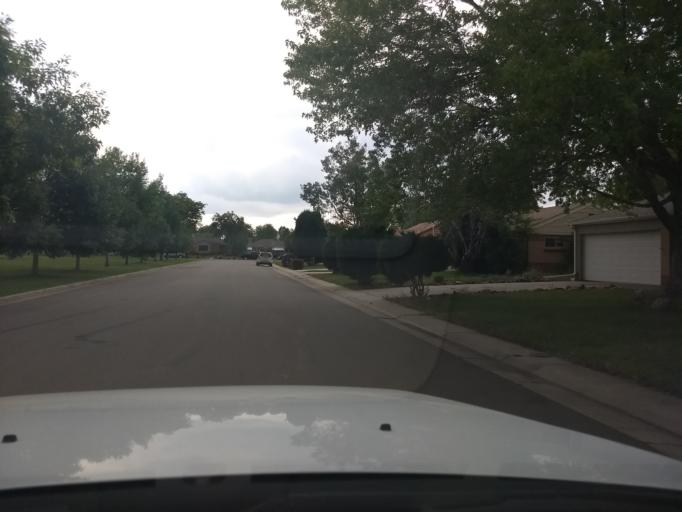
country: US
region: Colorado
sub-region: Denver County
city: Denver
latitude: 39.7000
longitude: -105.0155
